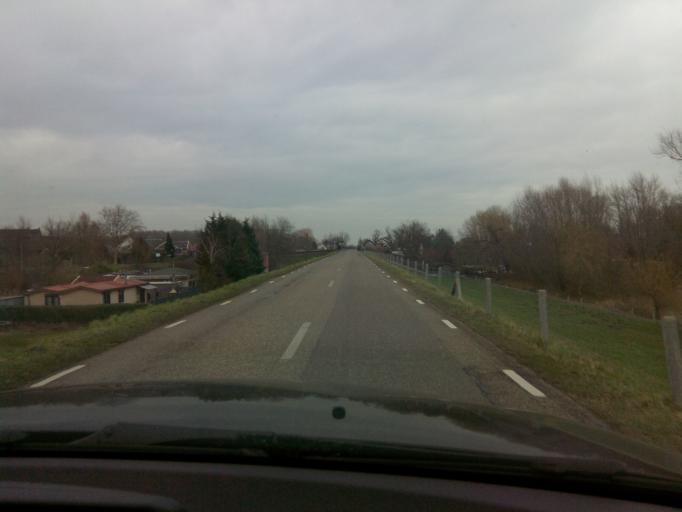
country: NL
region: South Holland
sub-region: Gemeente Leerdam
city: Leerdam
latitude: 51.8764
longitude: 5.1142
